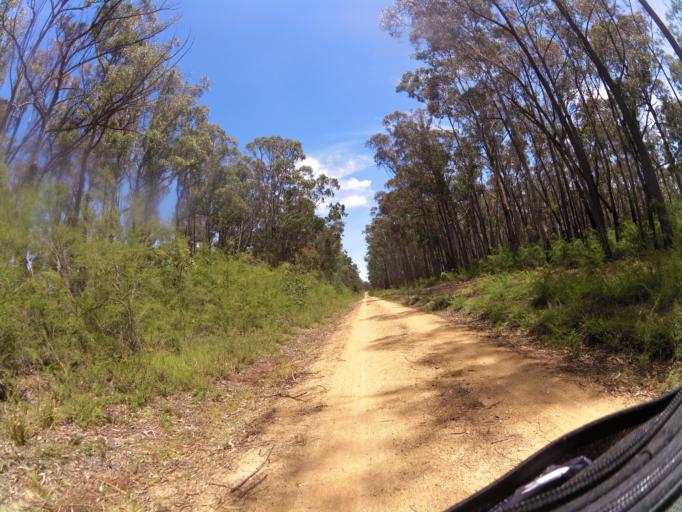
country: AU
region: Victoria
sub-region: East Gippsland
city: Lakes Entrance
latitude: -37.7571
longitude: 147.9627
